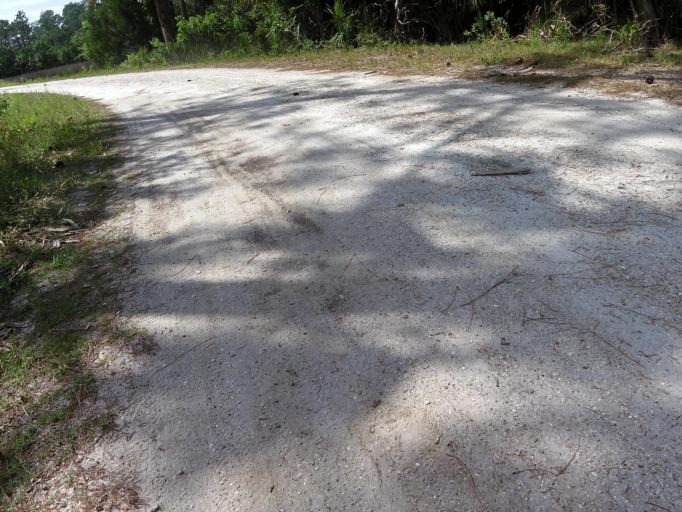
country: US
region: Florida
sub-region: Saint Johns County
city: Palm Valley
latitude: 30.1372
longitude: -81.3690
